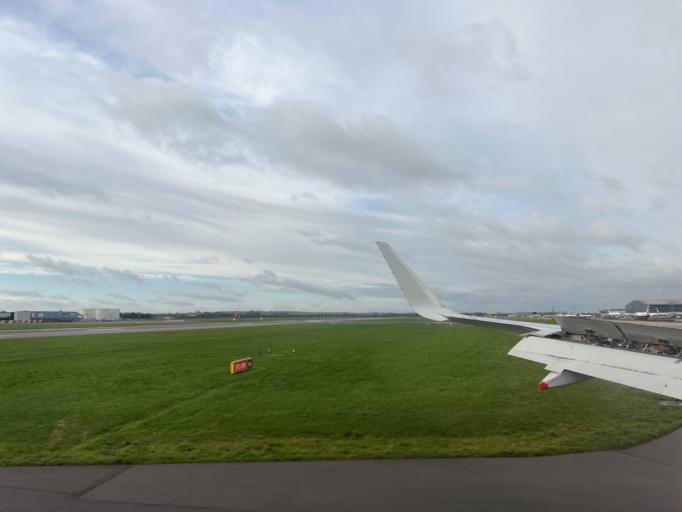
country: GB
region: England
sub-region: Greater London
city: West Drayton
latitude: 51.4662
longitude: -0.4687
